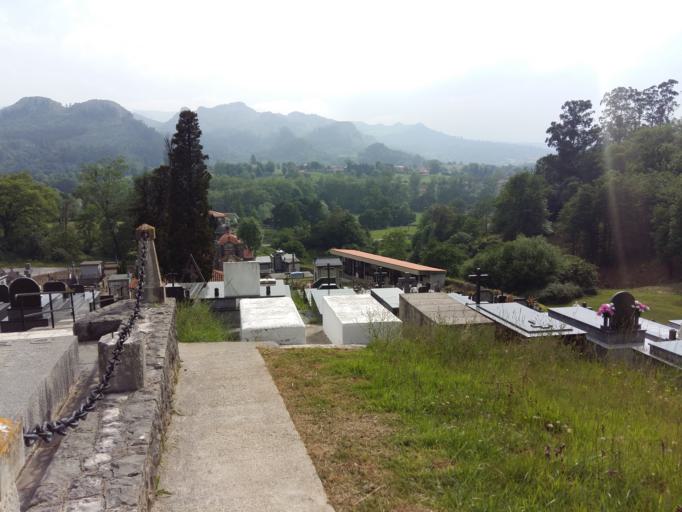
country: ES
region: Cantabria
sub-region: Provincia de Cantabria
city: Entrambasaguas
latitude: 43.3492
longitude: -3.6918
